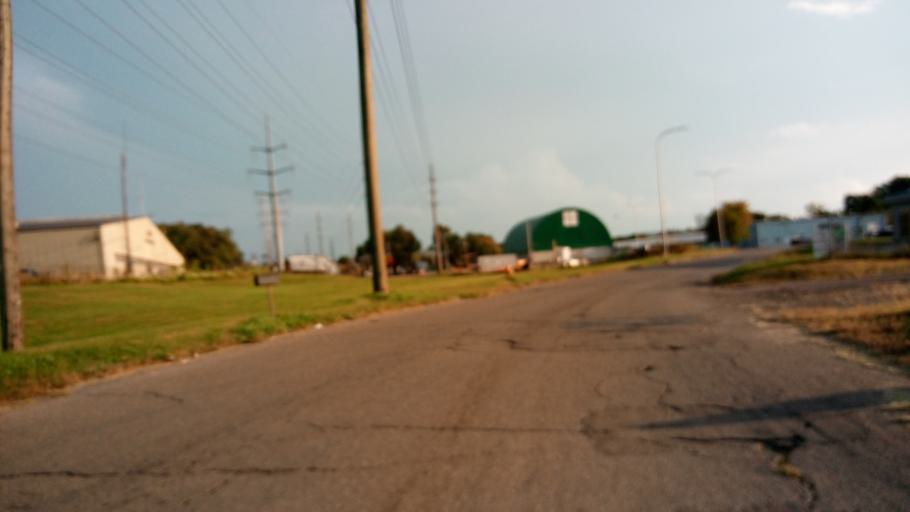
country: US
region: New York
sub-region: Chemung County
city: Elmira
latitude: 42.1079
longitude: -76.7975
